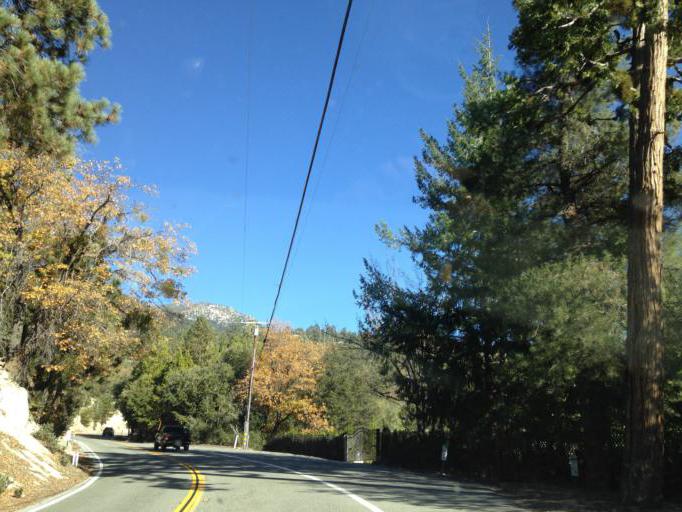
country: US
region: California
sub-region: Riverside County
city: Idyllwild-Pine Cove
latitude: 33.7787
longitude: -116.7433
